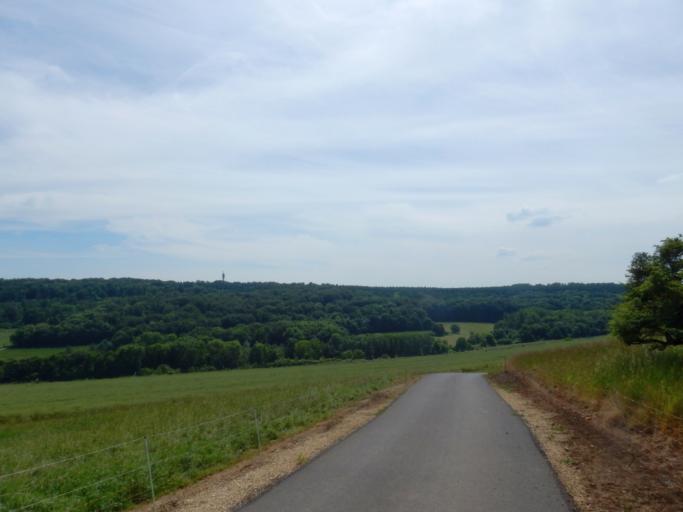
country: FR
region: Lorraine
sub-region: Departement de Meurthe-et-Moselle
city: Pagny-sur-Moselle
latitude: 48.9750
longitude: 5.9863
